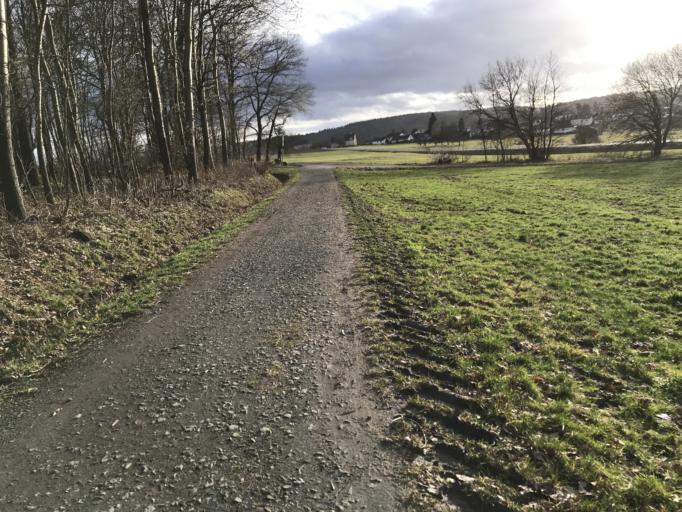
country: DE
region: Hesse
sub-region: Regierungsbezirk Giessen
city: Heuchelheim
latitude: 50.6307
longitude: 8.5978
